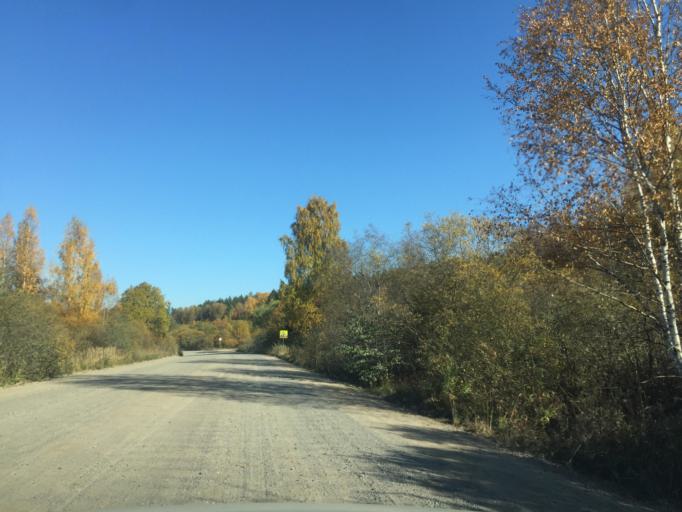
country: RU
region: Leningrad
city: Kuznechnoye
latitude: 61.3114
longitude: 29.9405
